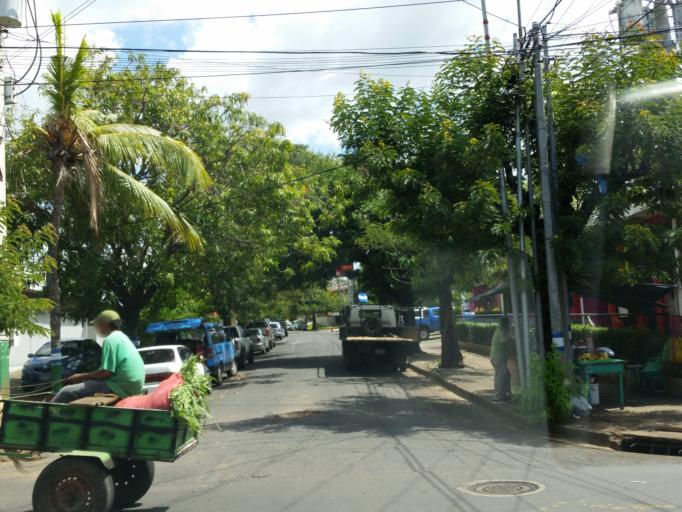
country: NI
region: Managua
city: Managua
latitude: 12.1198
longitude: -86.2582
